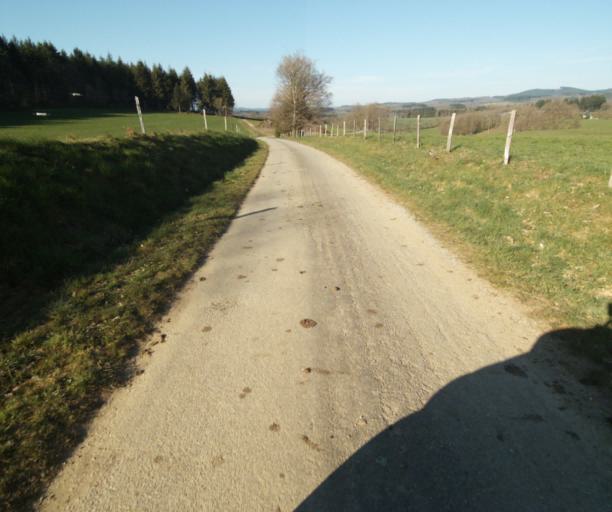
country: FR
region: Limousin
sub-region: Departement de la Correze
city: Chamboulive
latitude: 45.4780
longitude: 1.7271
